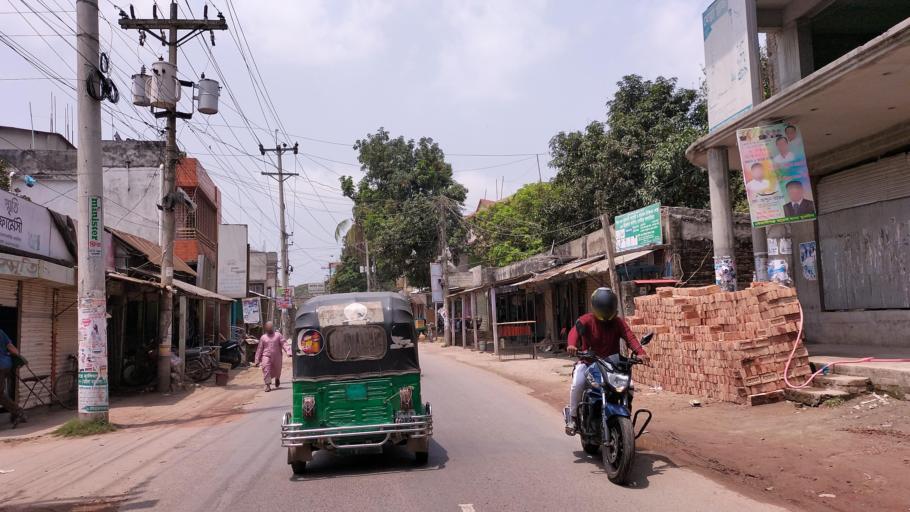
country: BD
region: Dhaka
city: Azimpur
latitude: 23.7308
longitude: 90.2765
